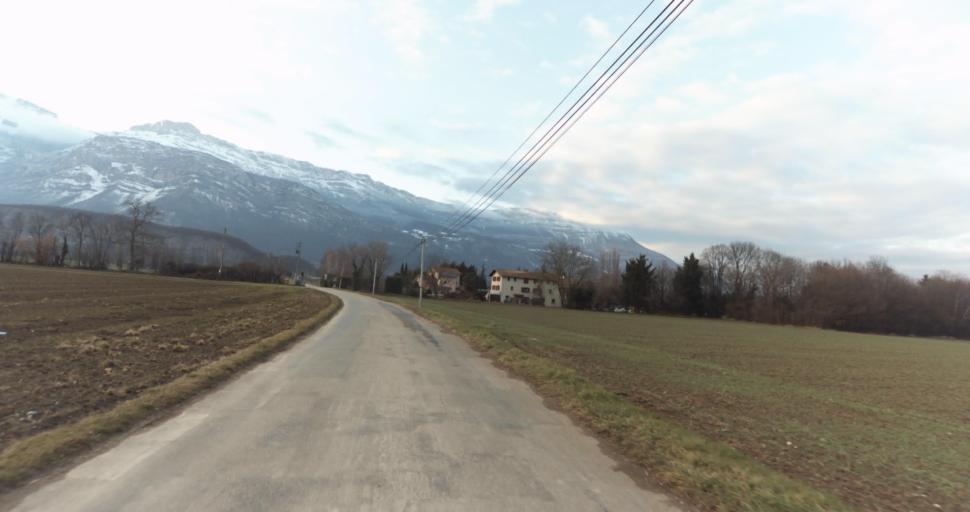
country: FR
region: Rhone-Alpes
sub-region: Departement de l'Isere
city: Allieres-et-Risset
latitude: 45.0809
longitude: 5.6969
